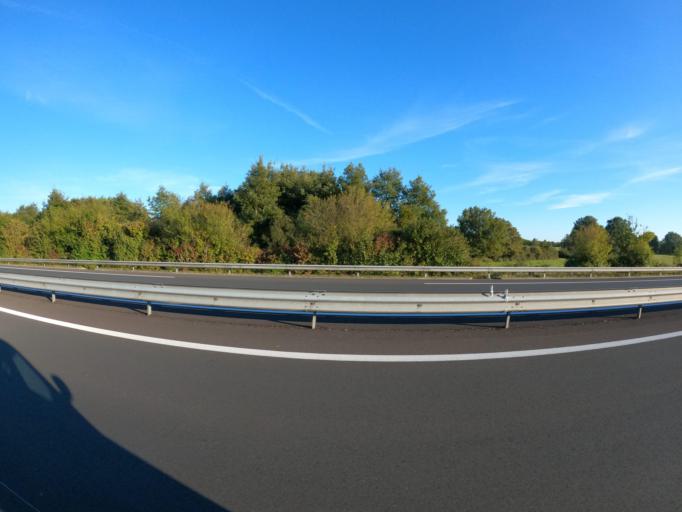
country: FR
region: Pays de la Loire
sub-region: Departement de la Vendee
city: Vendrennes
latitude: 46.8644
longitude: -1.1365
